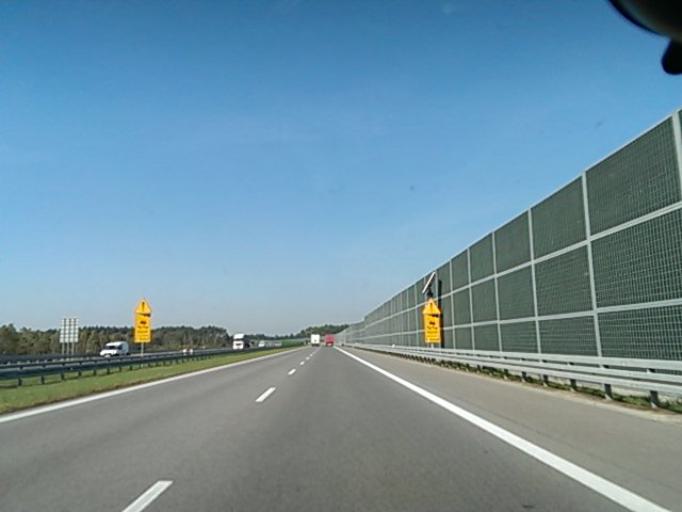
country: PL
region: Subcarpathian Voivodeship
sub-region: Powiat rzeszowski
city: Trzciana
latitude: 50.1166
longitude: 21.8135
